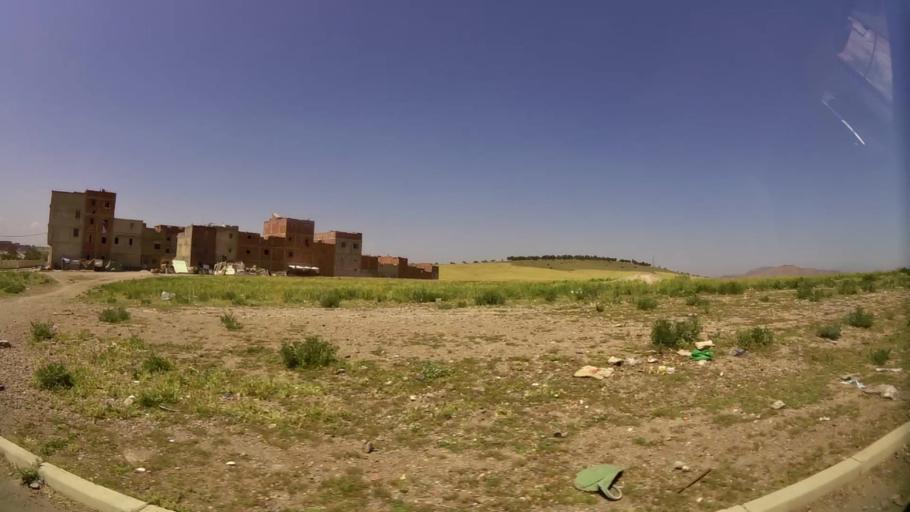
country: MA
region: Oriental
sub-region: Oujda-Angad
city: Oujda
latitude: 34.6800
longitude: -1.9599
